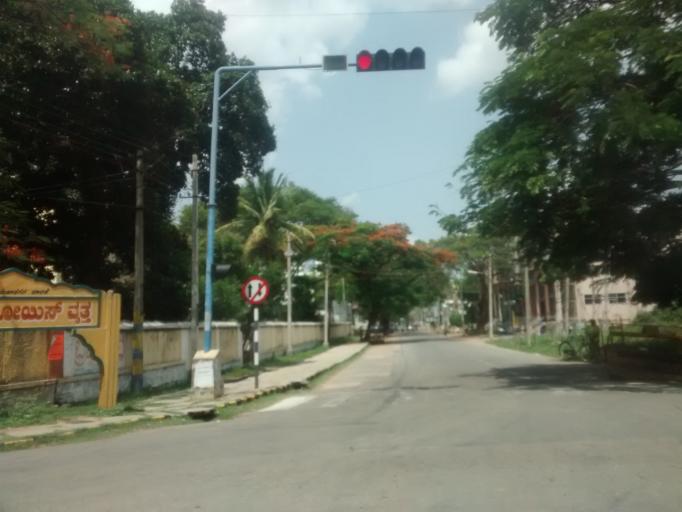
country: IN
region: Karnataka
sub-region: Mysore
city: Mysore
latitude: 12.3065
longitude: 76.6439
